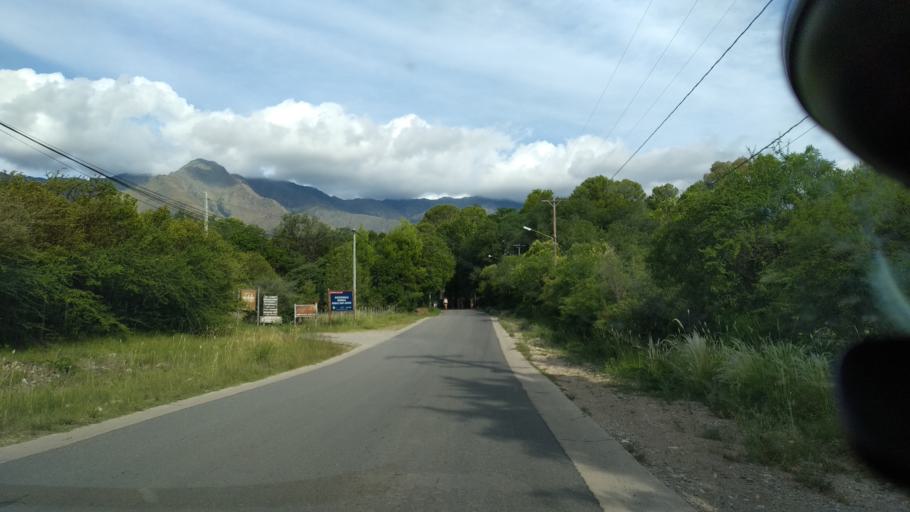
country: AR
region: Cordoba
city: Villa Las Rosas
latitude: -32.0264
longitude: -65.0142
